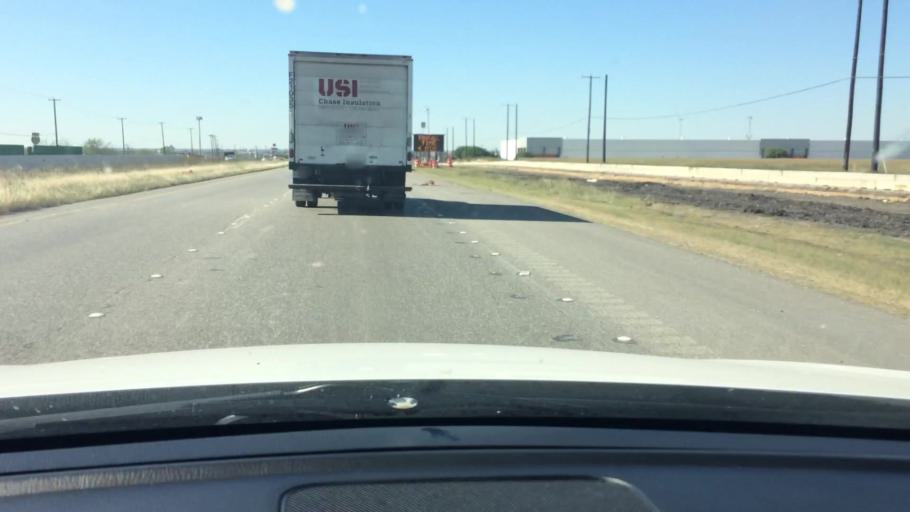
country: US
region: Texas
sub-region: Bexar County
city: Kirby
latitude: 29.4471
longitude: -98.3537
